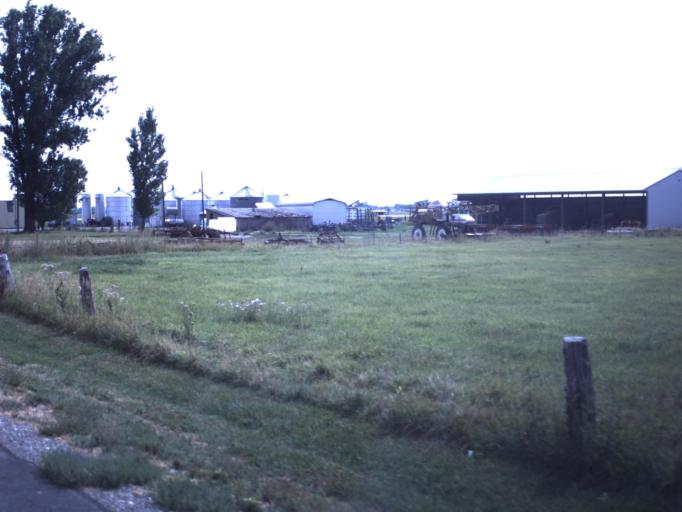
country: US
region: Utah
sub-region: Box Elder County
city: Garland
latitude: 41.8066
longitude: -112.1160
